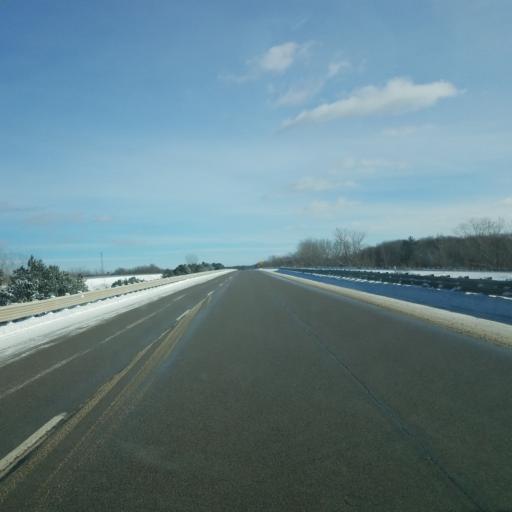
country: US
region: Michigan
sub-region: Clare County
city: Clare
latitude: 43.8649
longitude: -84.9086
